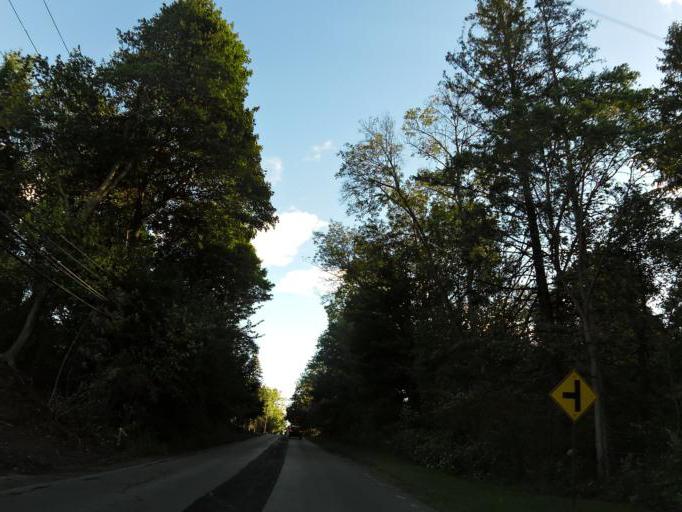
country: US
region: New York
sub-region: Erie County
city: Billington Heights
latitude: 42.7813
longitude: -78.6208
